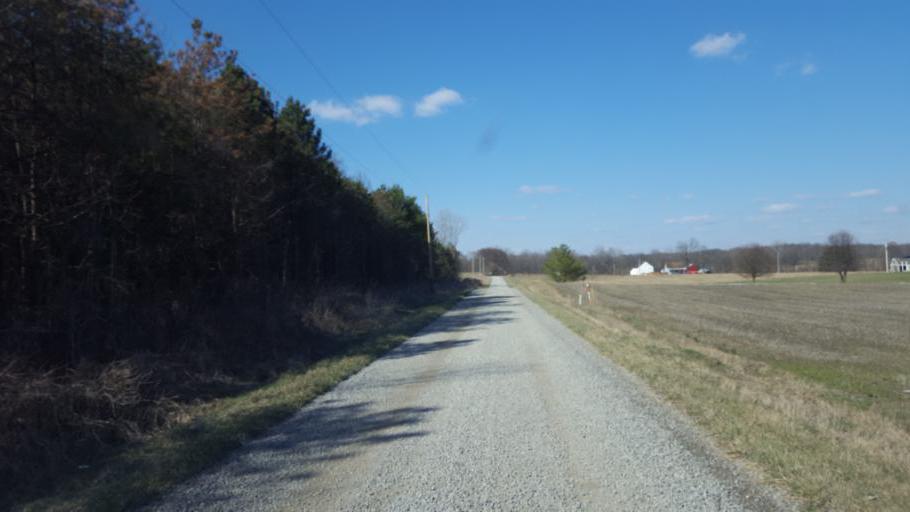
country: US
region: Ohio
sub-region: Morrow County
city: Mount Gilead
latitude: 40.4709
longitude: -82.7445
